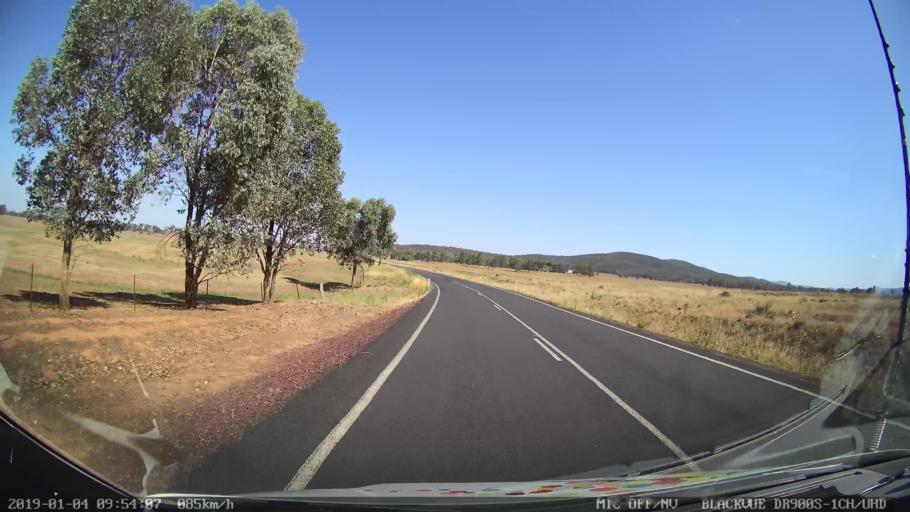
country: AU
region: New South Wales
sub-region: Cabonne
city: Canowindra
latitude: -33.5442
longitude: 148.4185
